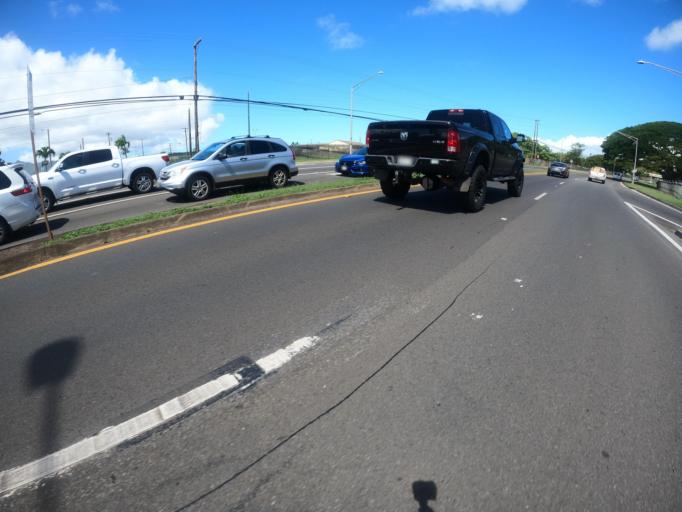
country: US
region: Hawaii
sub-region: Honolulu County
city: Schofield Barracks
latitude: 21.4829
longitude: -158.0476
